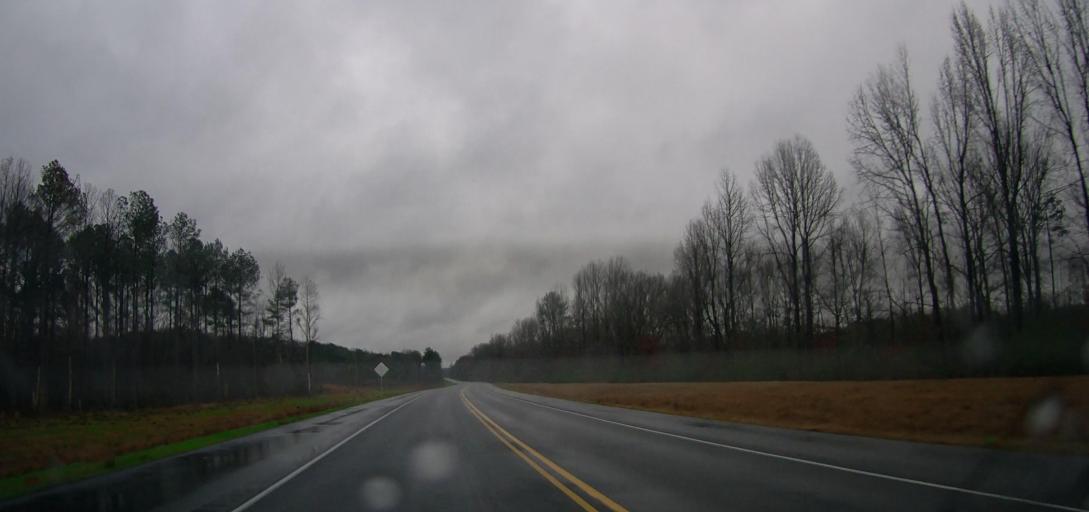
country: US
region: Alabama
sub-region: Bibb County
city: Centreville
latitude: 32.9312
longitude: -87.0553
